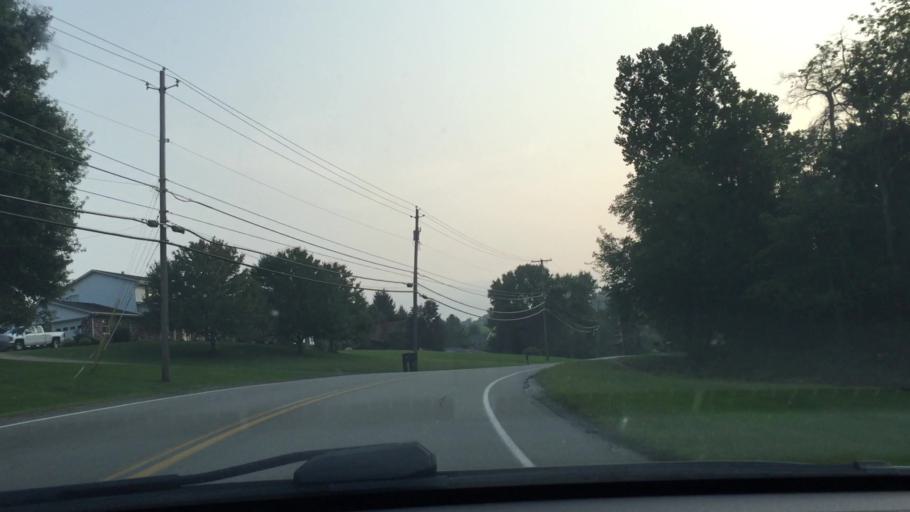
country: US
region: Pennsylvania
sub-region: Westmoreland County
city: Fellsburg
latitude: 40.1693
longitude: -79.8112
